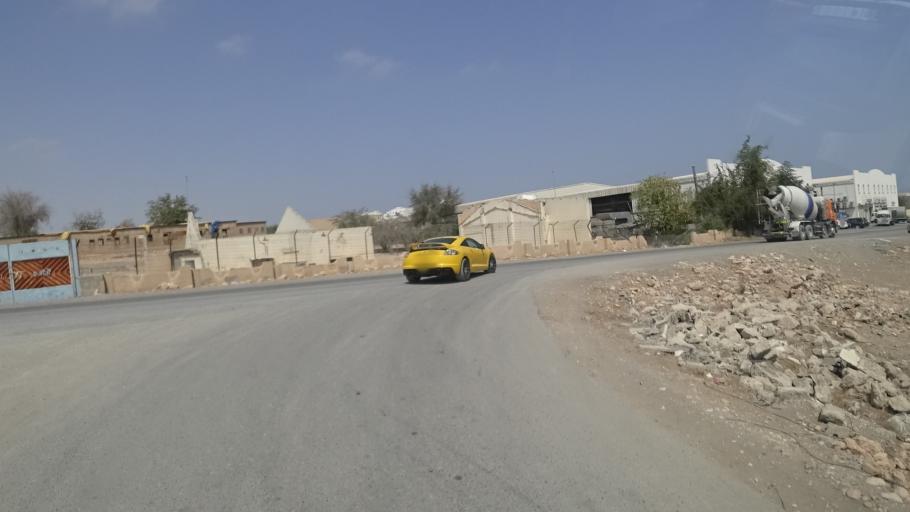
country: OM
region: Muhafazat Masqat
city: Bawshar
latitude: 23.5729
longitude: 58.3465
